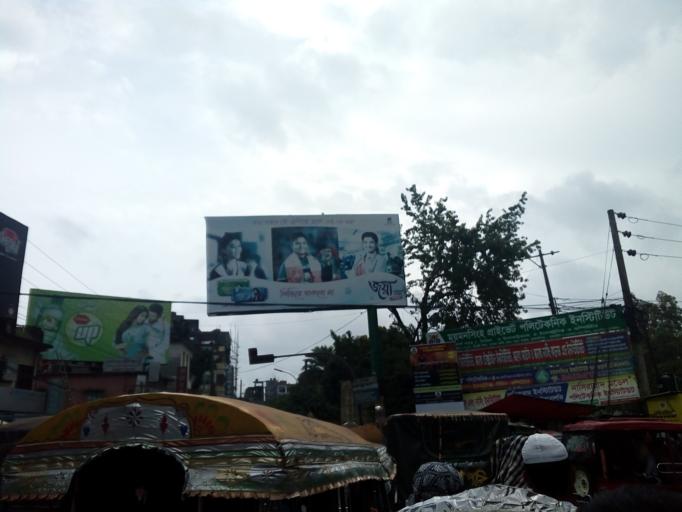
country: BD
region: Dhaka
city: Mymensingh
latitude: 24.7466
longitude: 90.4092
